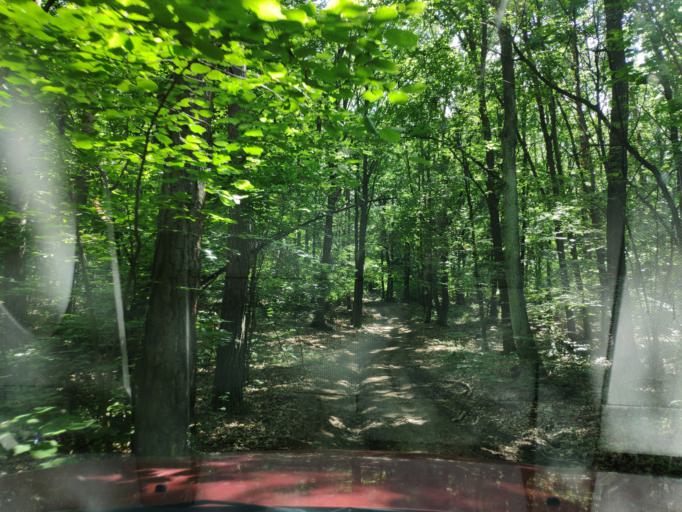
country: SK
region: Presovsky
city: Vranov nad Topl'ou
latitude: 48.8190
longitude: 21.6030
